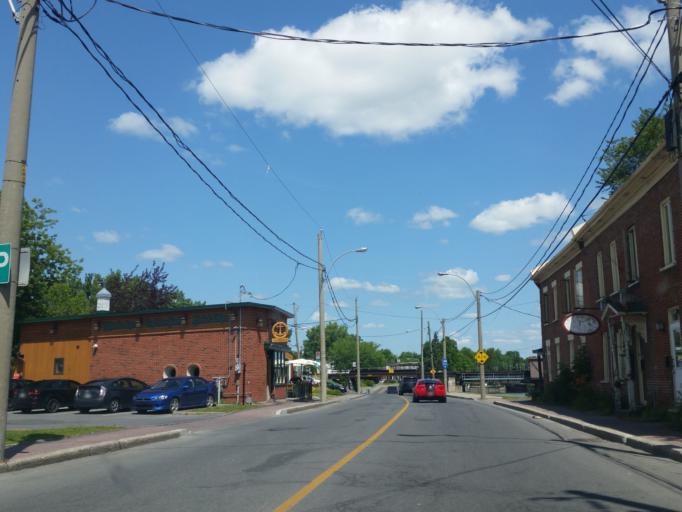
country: CA
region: Quebec
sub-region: Monteregie
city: Saint-Jean-sur-Richelieu
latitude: 45.3086
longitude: -73.2509
